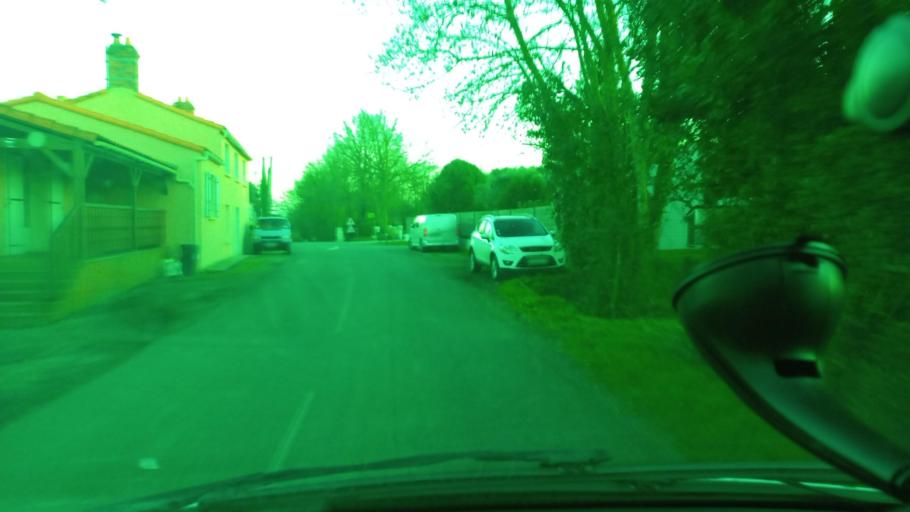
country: FR
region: Pays de la Loire
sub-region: Departement de la Vendee
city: Belleville-sur-Vie
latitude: 46.7947
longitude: -1.4115
